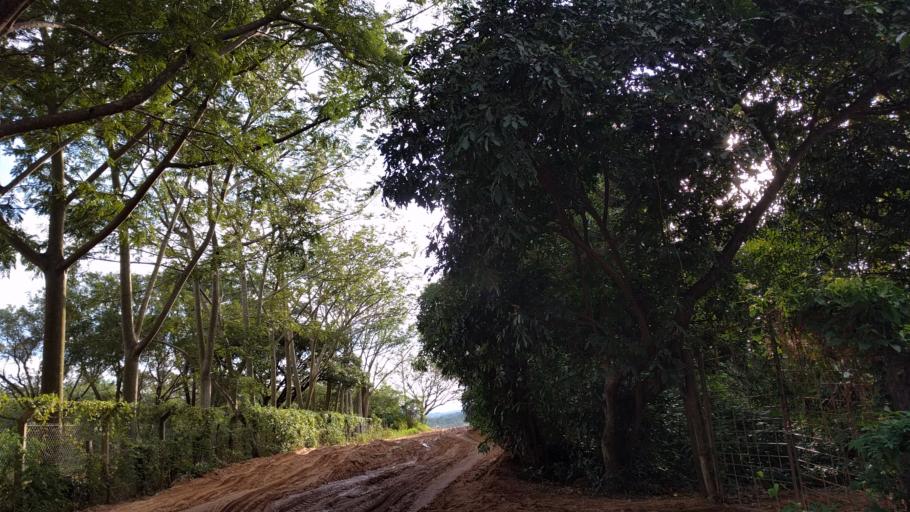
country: BO
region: Santa Cruz
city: Santa Cruz de la Sierra
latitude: -17.8535
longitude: -63.2783
